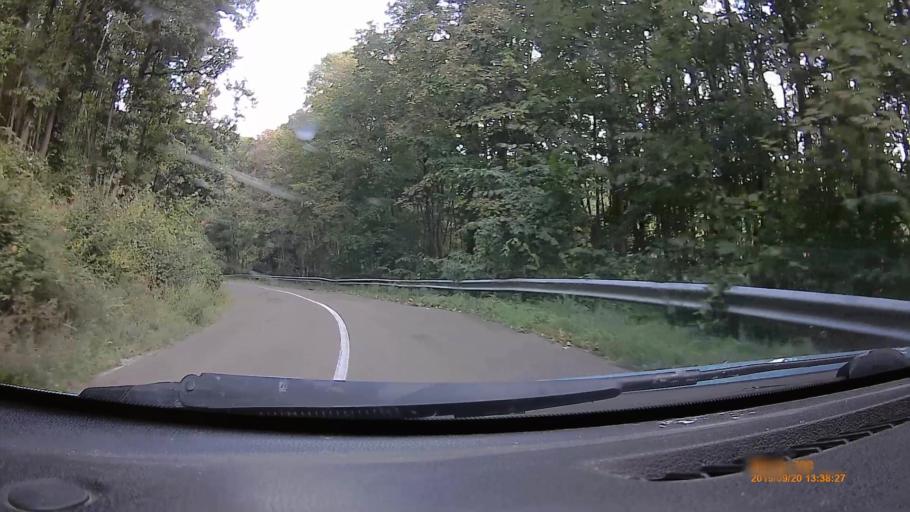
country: HU
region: Heves
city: Szilvasvarad
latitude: 48.0603
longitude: 20.5249
